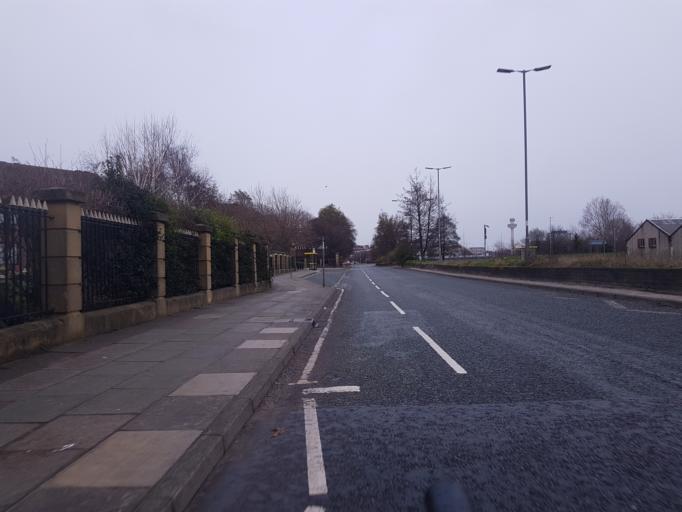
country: GB
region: England
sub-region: Liverpool
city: Liverpool
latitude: 53.4199
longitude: -2.9780
